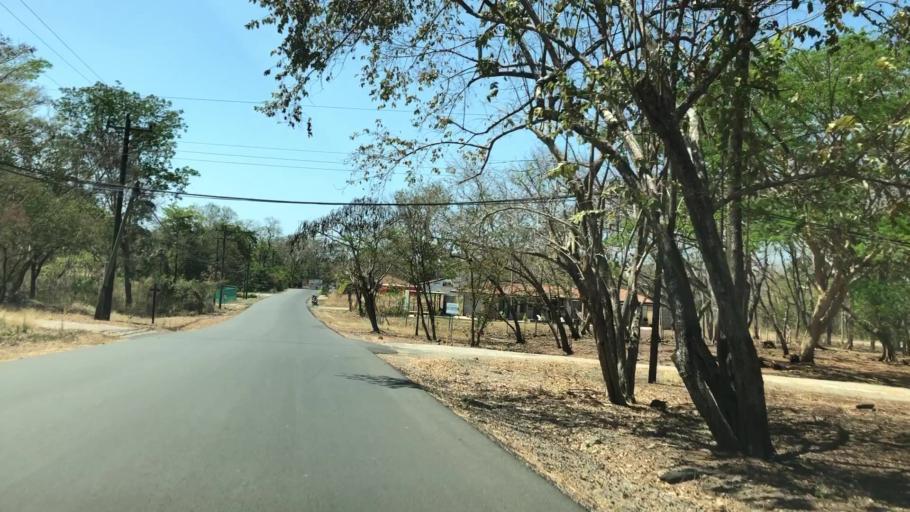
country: CR
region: Guanacaste
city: Sardinal
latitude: 10.3387
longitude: -85.8458
